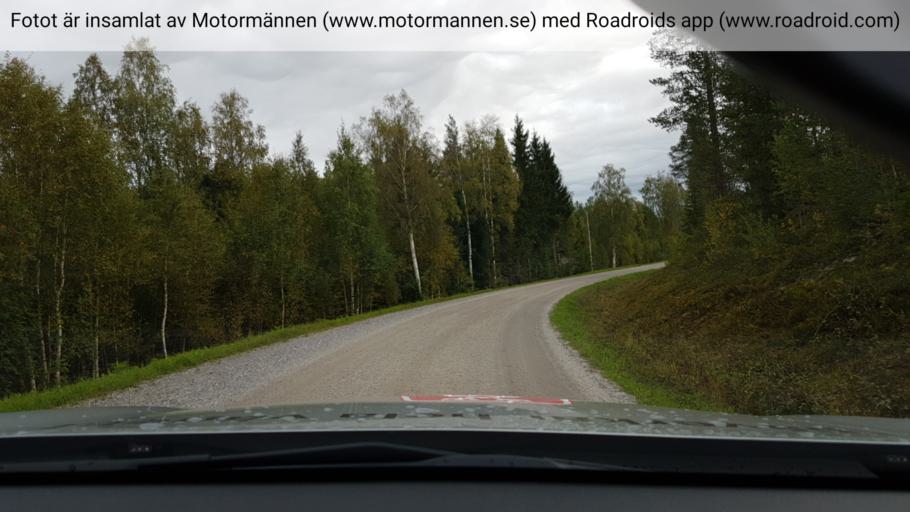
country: SE
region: Vaesterbotten
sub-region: Skelleftea Kommun
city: Byske
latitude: 65.1097
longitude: 21.1867
